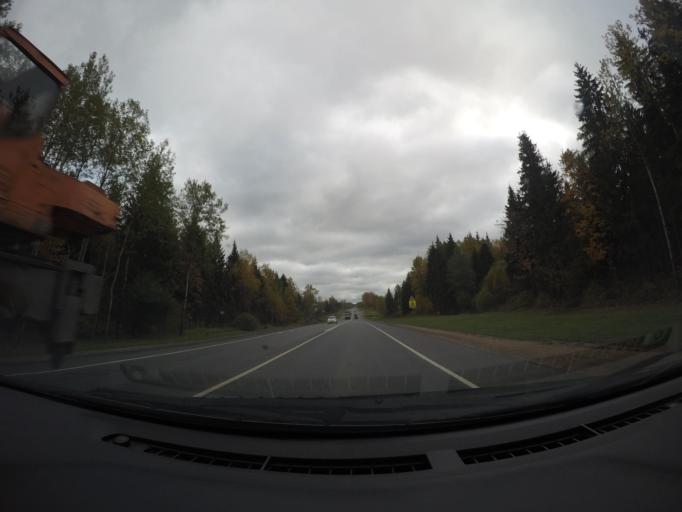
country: RU
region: Moskovskaya
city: Dorokhovo
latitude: 55.6003
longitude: 36.3591
